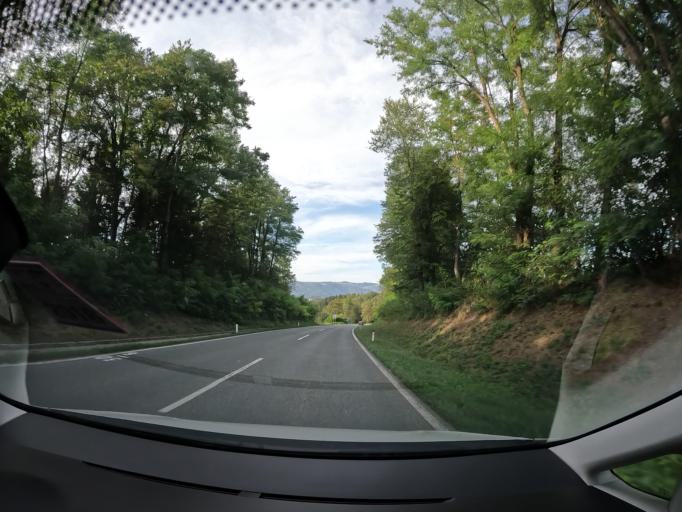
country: AT
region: Carinthia
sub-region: Politischer Bezirk Volkermarkt
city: Voelkermarkt
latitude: 46.6397
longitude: 14.6295
